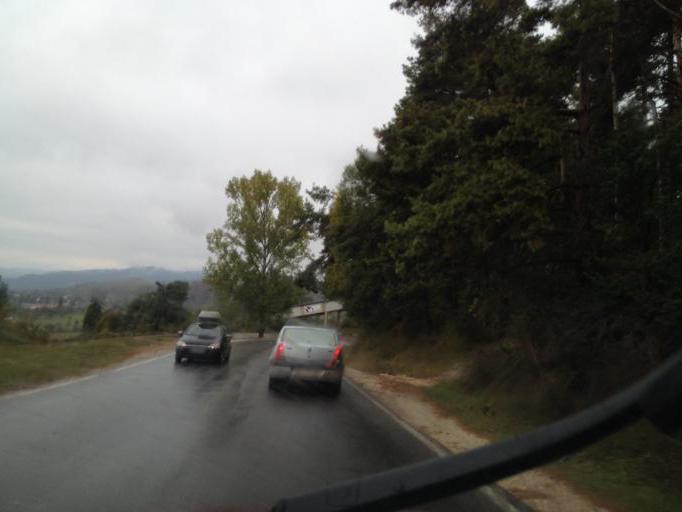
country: RO
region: Arges
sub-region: Comuna Valea Mare-Pravat
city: Valea Mare Pravat
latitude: 45.2966
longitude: 25.1280
